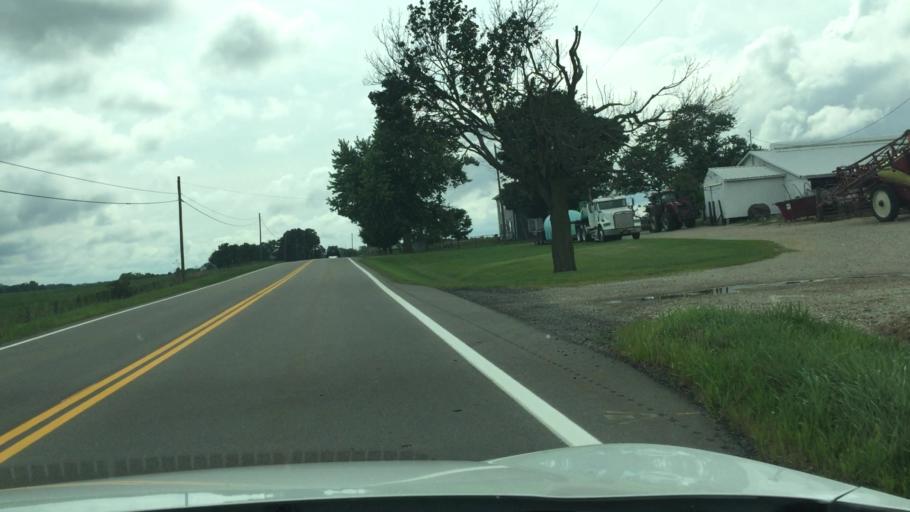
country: US
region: Ohio
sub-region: Clark County
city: Northridge
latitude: 40.0181
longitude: -83.6761
